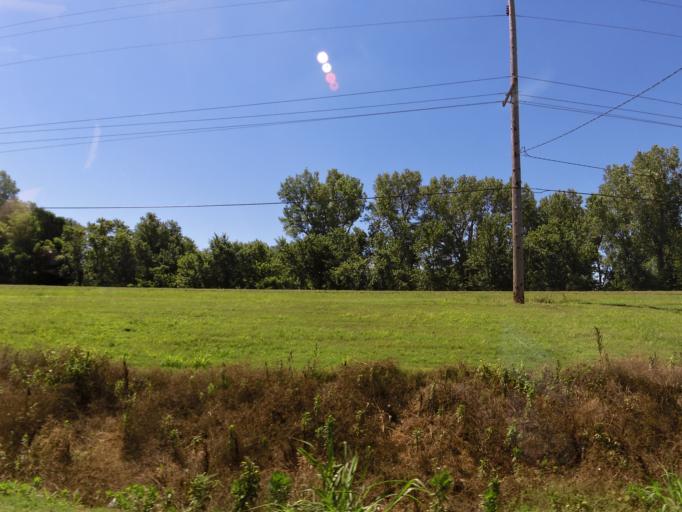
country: US
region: Missouri
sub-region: New Madrid County
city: New Madrid
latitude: 36.5835
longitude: -89.5442
